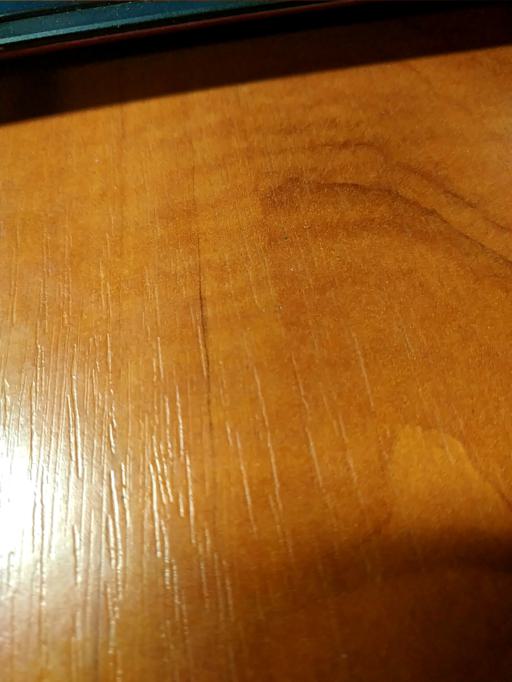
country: RU
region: Tverskaya
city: Likhoslavl'
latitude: 57.2854
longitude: 35.6181
